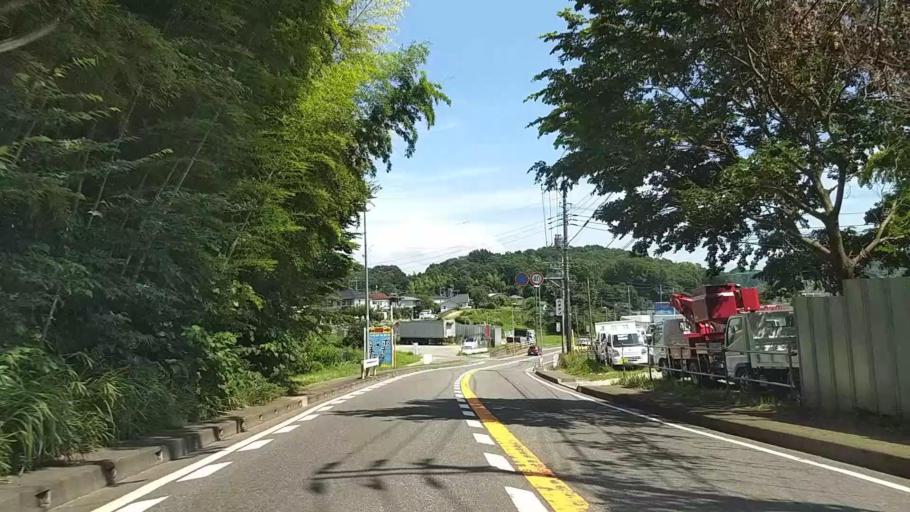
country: JP
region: Kanagawa
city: Fujisawa
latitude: 35.3712
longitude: 139.5162
